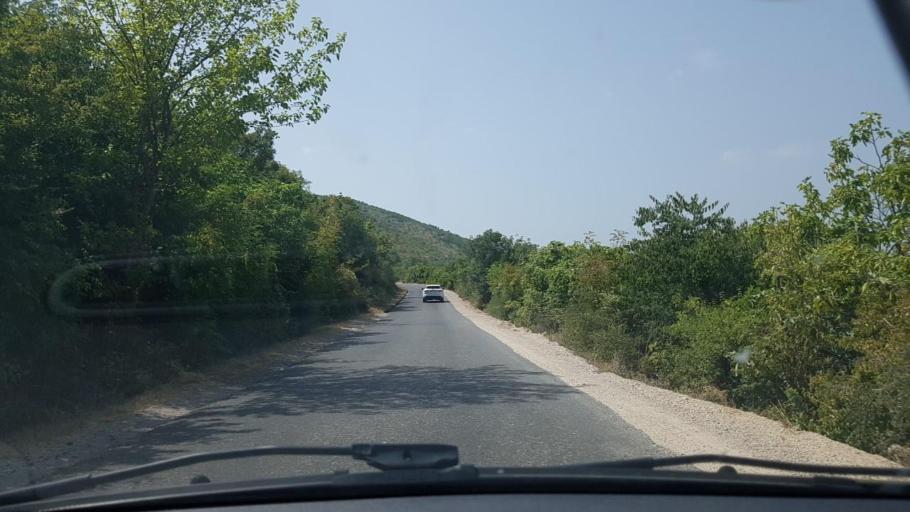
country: HR
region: Dubrovacko-Neretvanska
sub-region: Grad Dubrovnik
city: Metkovic
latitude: 43.0373
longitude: 17.7200
